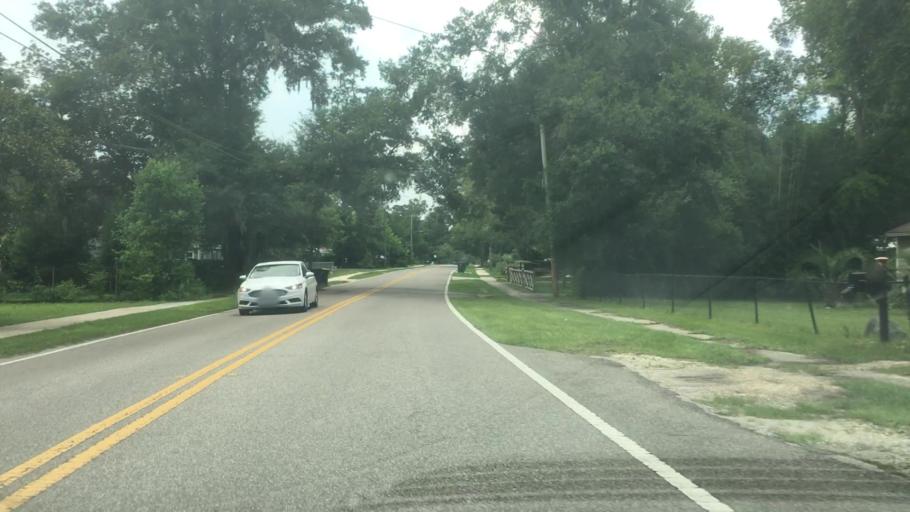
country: US
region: Florida
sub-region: Duval County
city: Jacksonville
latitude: 30.3018
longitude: -81.5493
